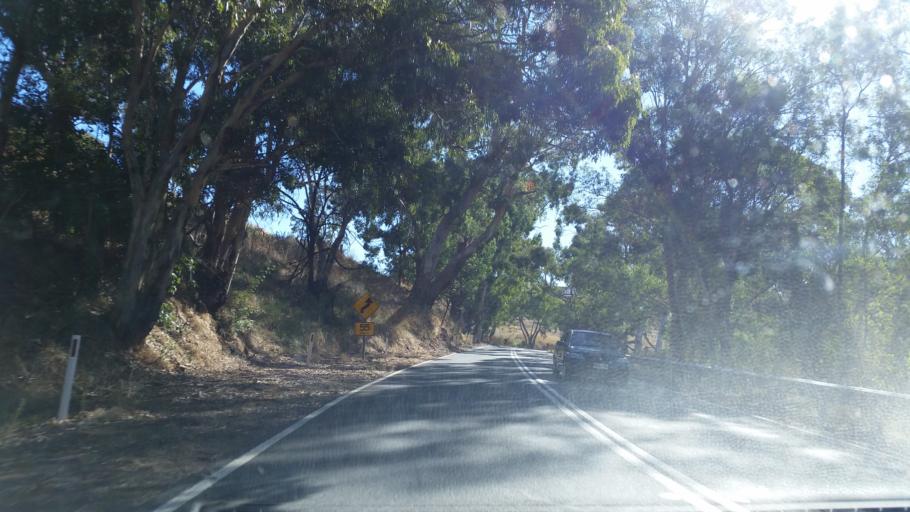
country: AU
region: South Australia
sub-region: Adelaide Hills
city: Birdwood
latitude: -34.8257
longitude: 138.9326
